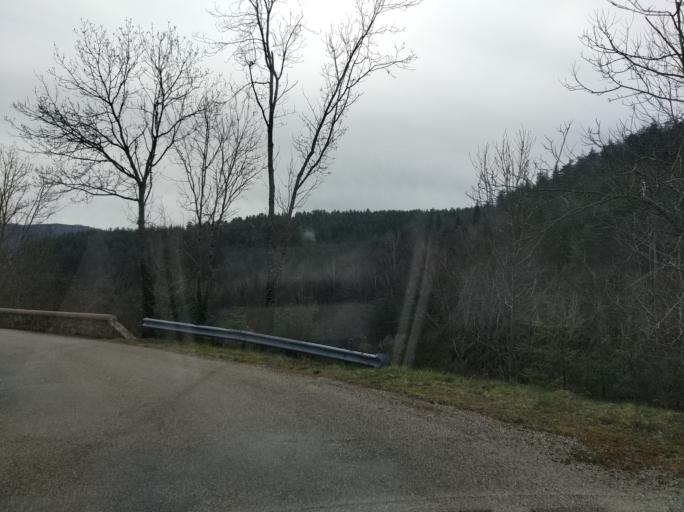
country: FR
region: Rhone-Alpes
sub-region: Departement de l'Ardeche
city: Satillieu
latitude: 45.1546
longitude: 4.5959
